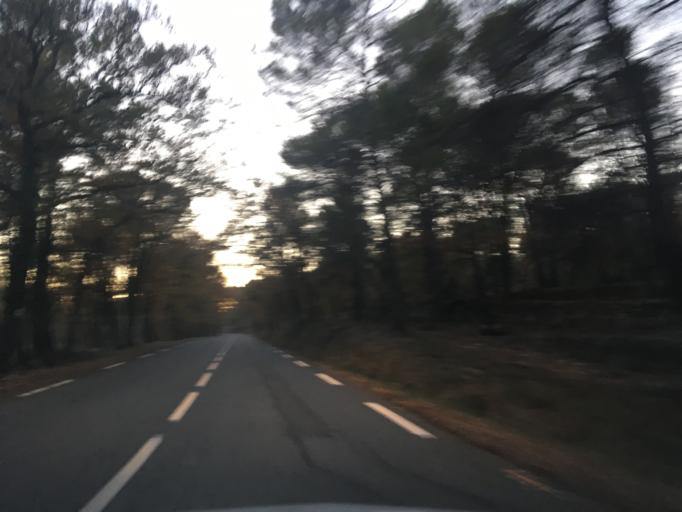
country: FR
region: Provence-Alpes-Cote d'Azur
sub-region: Departement du Var
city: Figanieres
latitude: 43.5379
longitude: 6.5181
